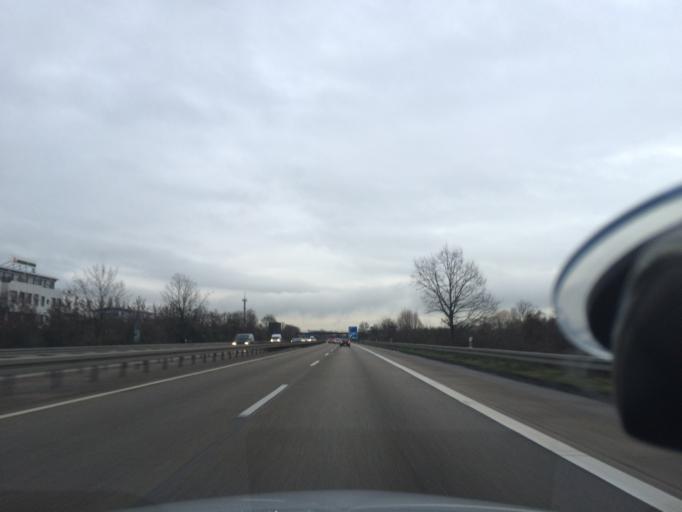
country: DE
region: Hesse
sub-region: Regierungsbezirk Darmstadt
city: Russelsheim
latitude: 49.9746
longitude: 8.4233
